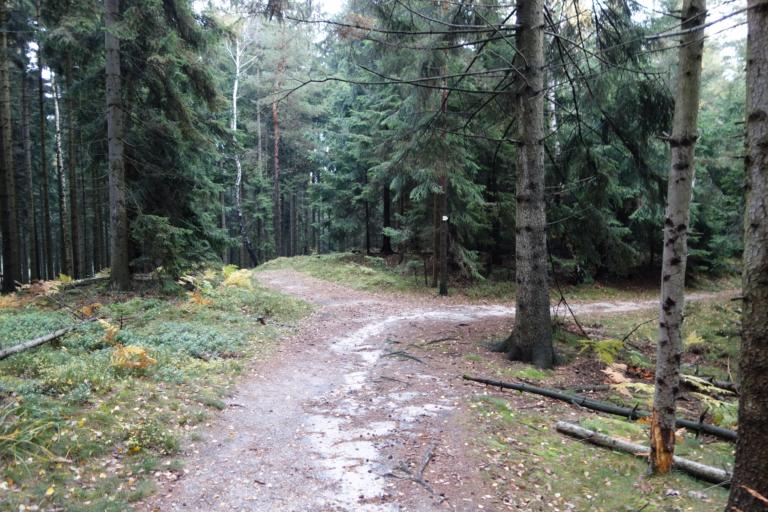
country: DE
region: Saxony
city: Kurort Oybin
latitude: 50.8473
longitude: 14.7370
